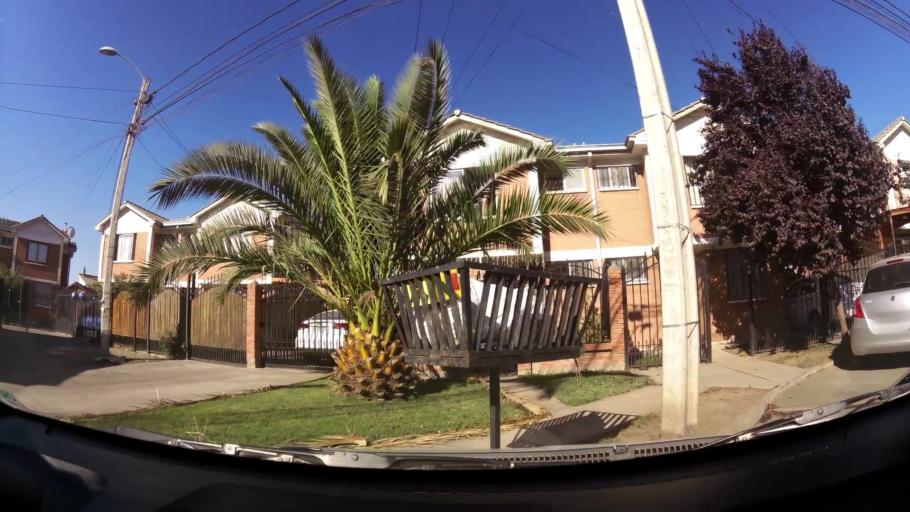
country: CL
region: O'Higgins
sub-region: Provincia de Cachapoal
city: Rancagua
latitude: -34.1784
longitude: -70.7584
